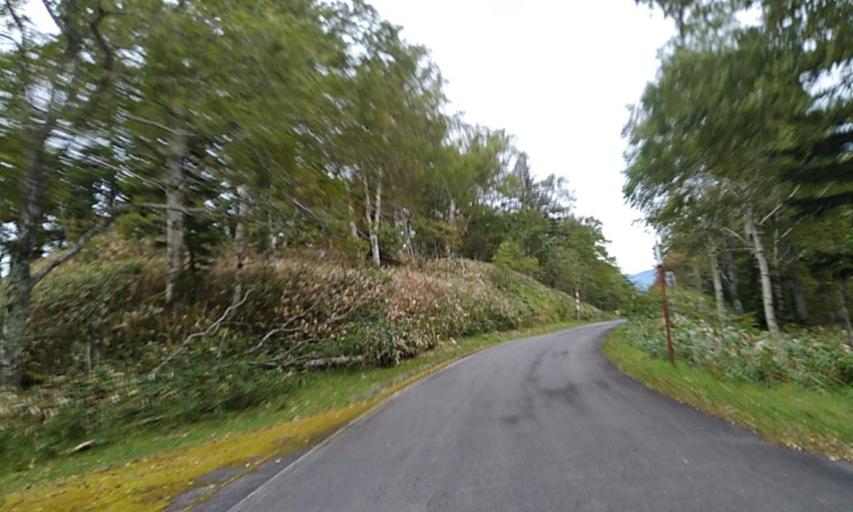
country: JP
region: Hokkaido
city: Bihoro
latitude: 43.5710
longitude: 144.2256
